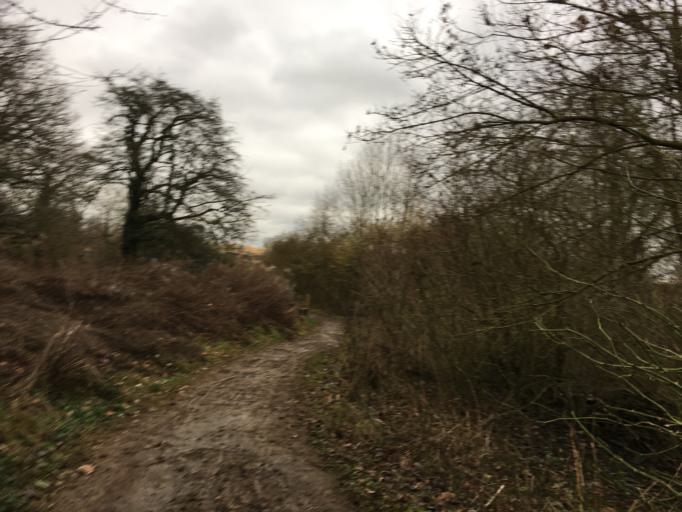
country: GB
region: England
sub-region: Warwickshire
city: Rugby
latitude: 52.3979
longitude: -1.2590
